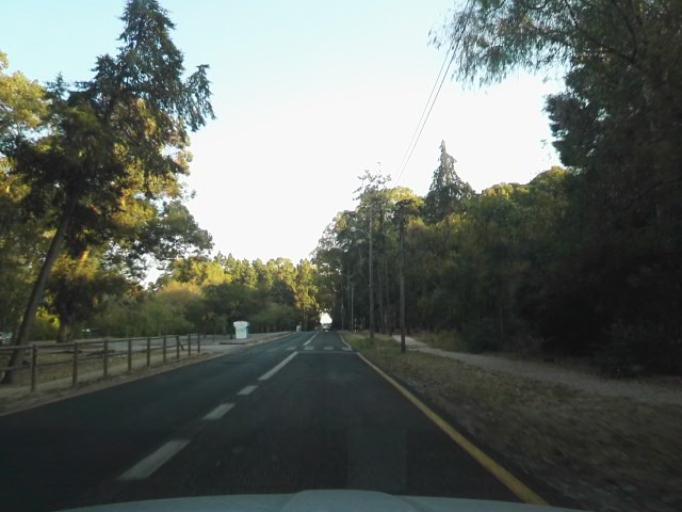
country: PT
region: Setubal
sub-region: Almada
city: Pragal
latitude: 38.7183
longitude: -9.1845
